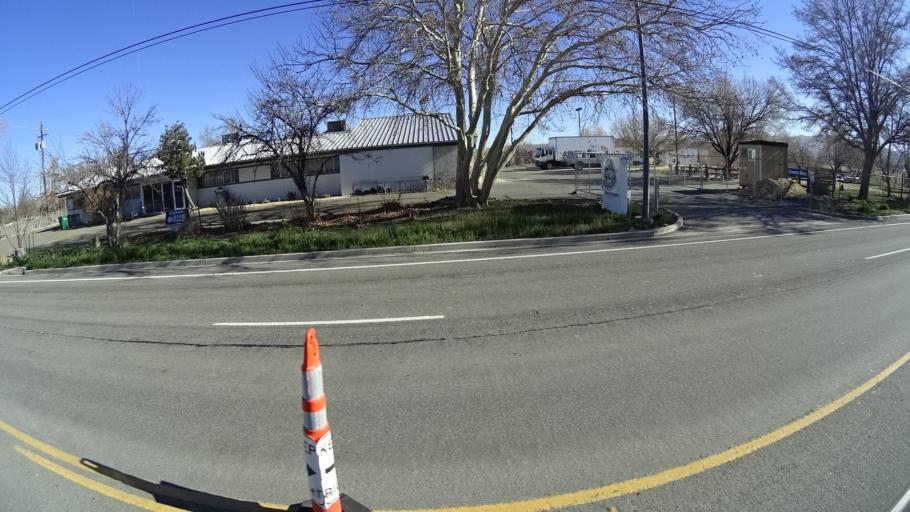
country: US
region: Nevada
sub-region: Washoe County
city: Sparks
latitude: 39.5136
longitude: -119.7500
